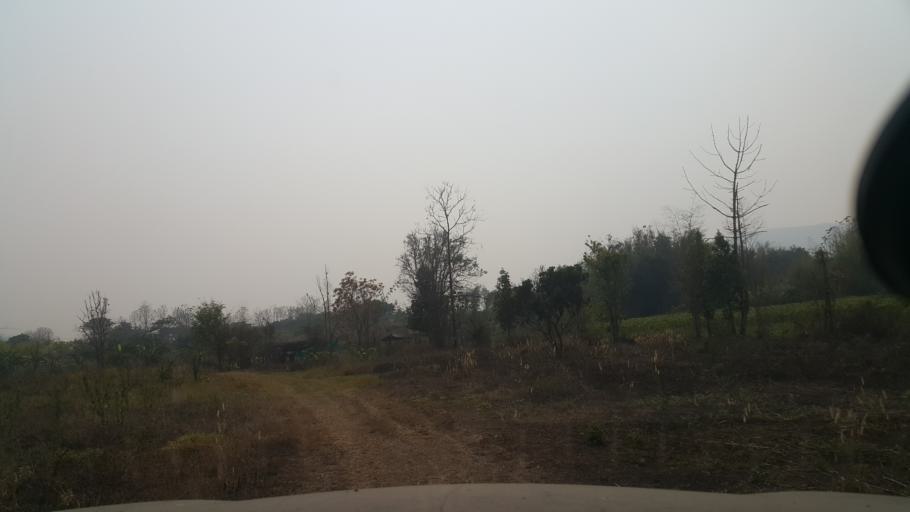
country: TH
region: Chiang Mai
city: Mae On
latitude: 18.7636
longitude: 99.2687
